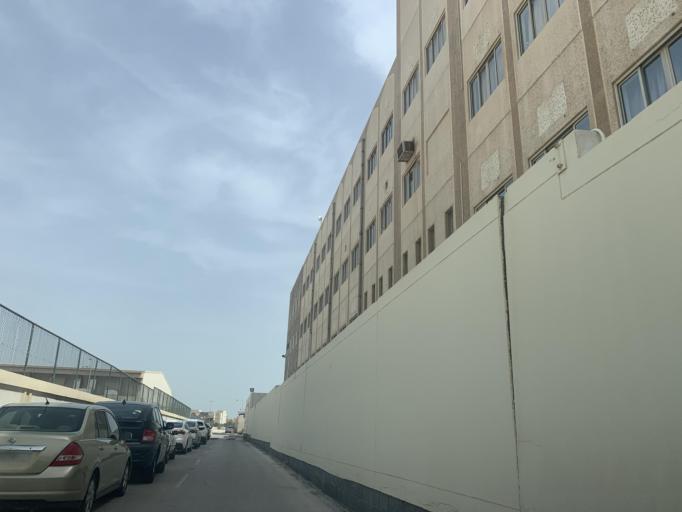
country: BH
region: Northern
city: Madinat `Isa
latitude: 26.1598
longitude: 50.5510
